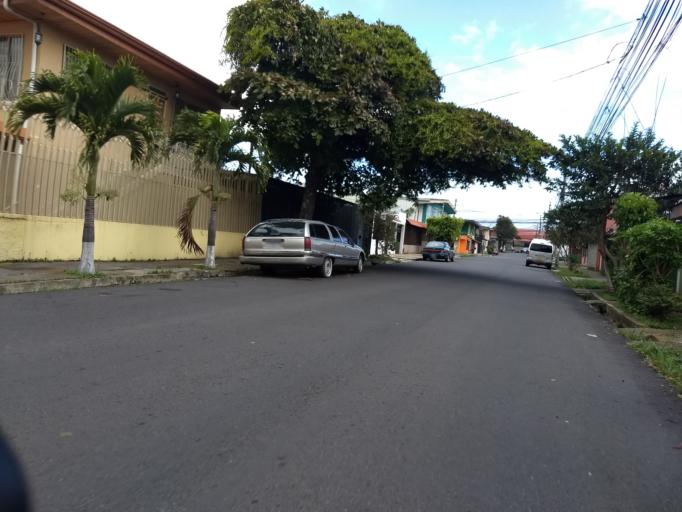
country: CR
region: San Jose
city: San Juan
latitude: 9.9617
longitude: -84.0836
